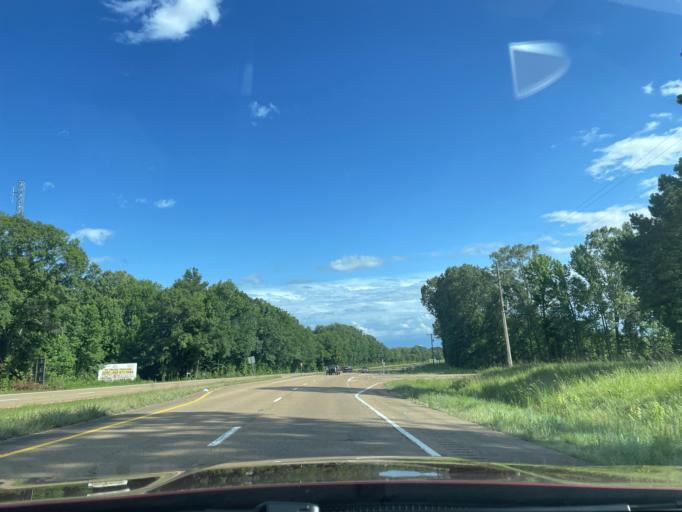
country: US
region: Mississippi
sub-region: Madison County
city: Flora
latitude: 32.4813
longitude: -90.2894
